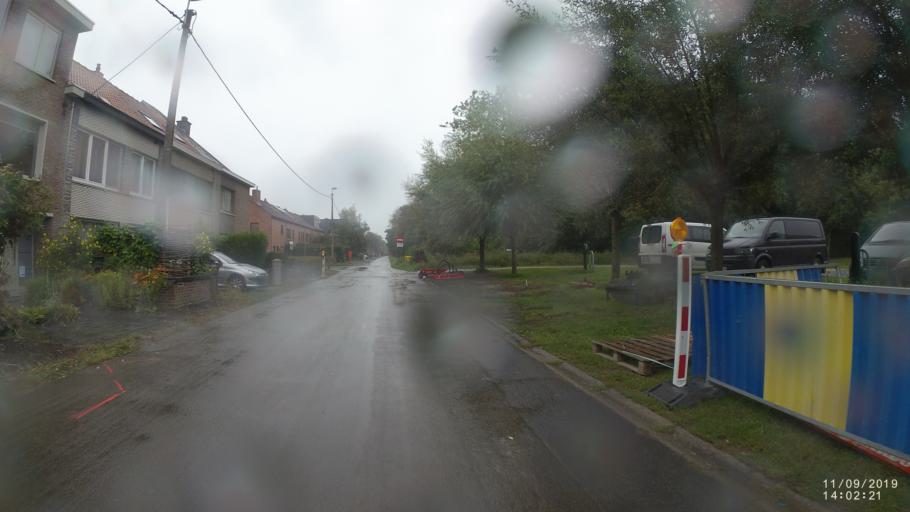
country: BE
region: Flanders
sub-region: Provincie Oost-Vlaanderen
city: Evergem
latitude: 51.0805
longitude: 3.6953
